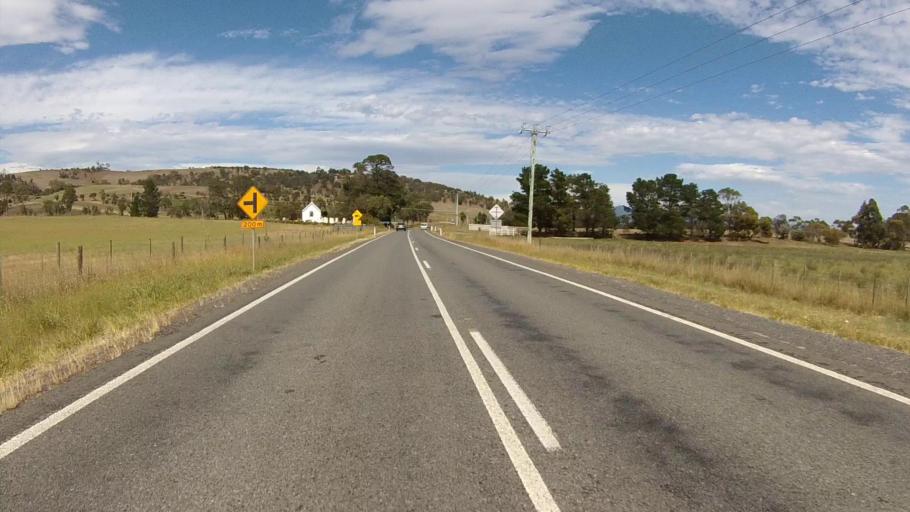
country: AU
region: Tasmania
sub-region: Brighton
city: Old Beach
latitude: -42.6904
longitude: 147.3464
